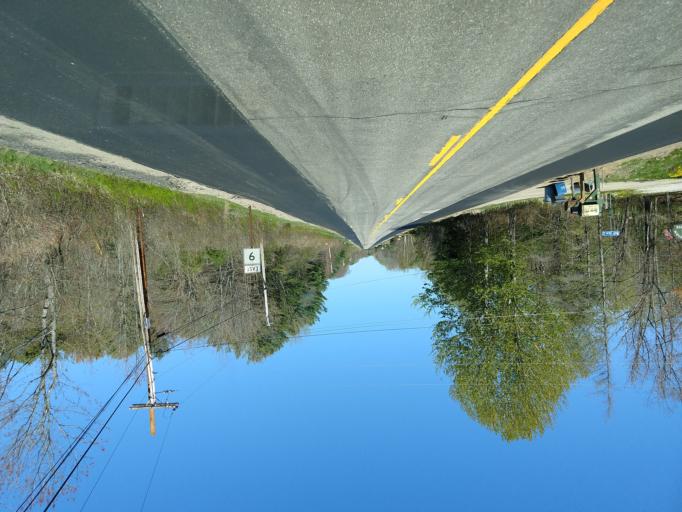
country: US
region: Maine
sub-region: York County
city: Arundel
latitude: 43.4135
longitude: -70.4143
